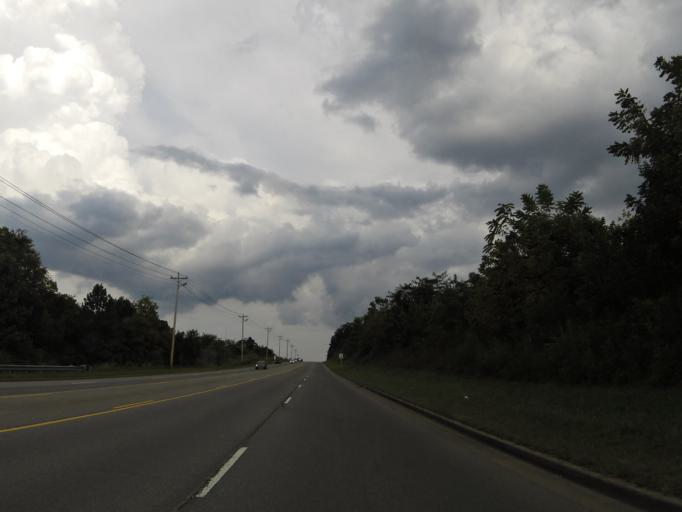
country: US
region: Tennessee
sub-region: Dickson County
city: Dickson
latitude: 36.0649
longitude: -87.3954
